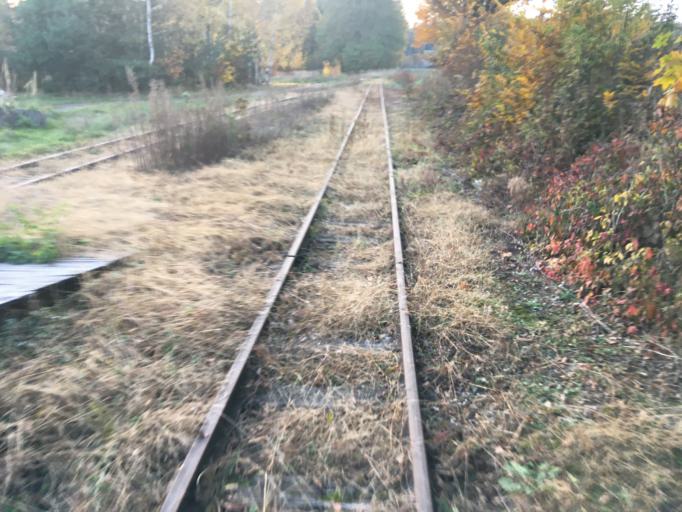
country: PL
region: Swietokrzyskie
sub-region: Powiat starachowicki
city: Starachowice
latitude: 51.0673
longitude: 21.1285
